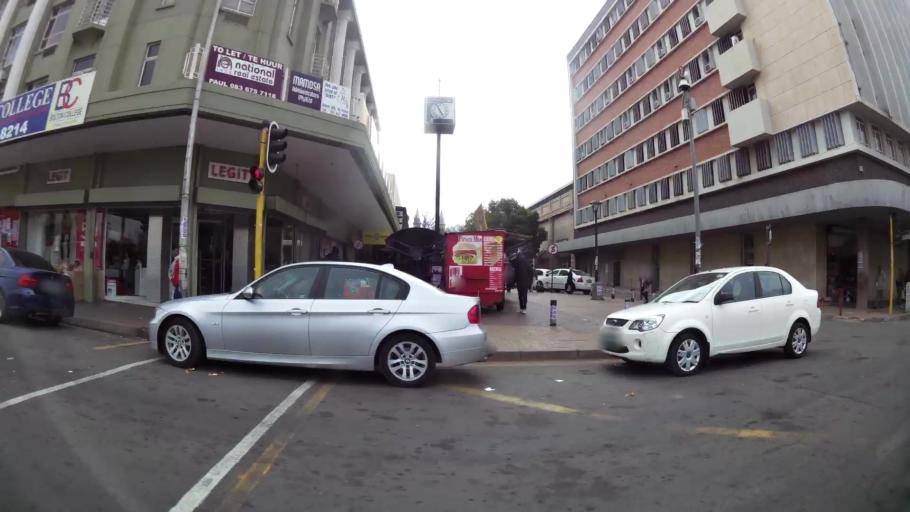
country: ZA
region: Orange Free State
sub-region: Mangaung Metropolitan Municipality
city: Bloemfontein
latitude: -29.1177
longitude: 26.2217
